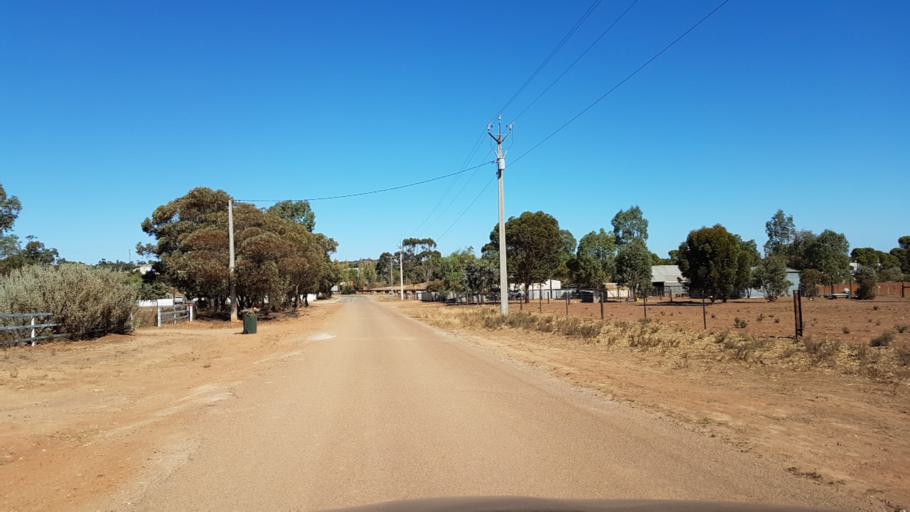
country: AU
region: South Australia
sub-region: Peterborough
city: Peterborough
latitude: -32.9699
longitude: 138.8257
